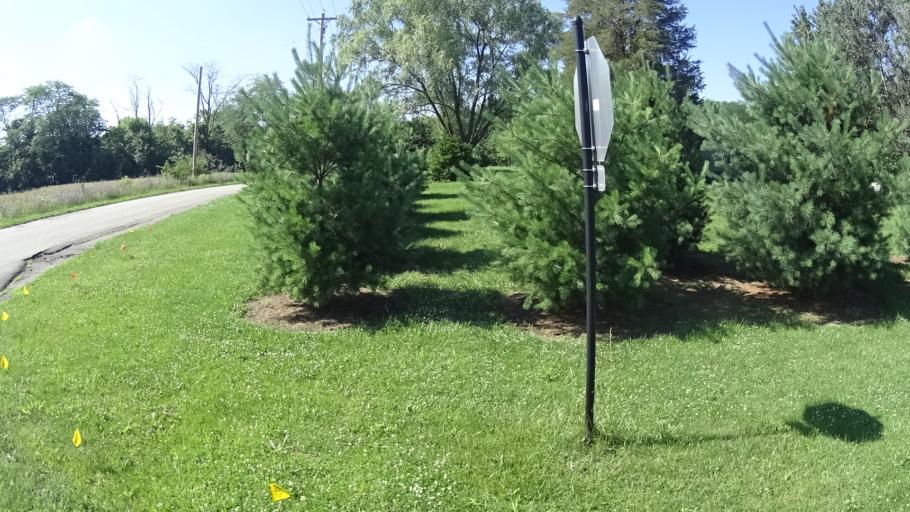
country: US
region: Indiana
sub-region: Madison County
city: Ingalls
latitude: 39.9768
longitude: -85.7964
